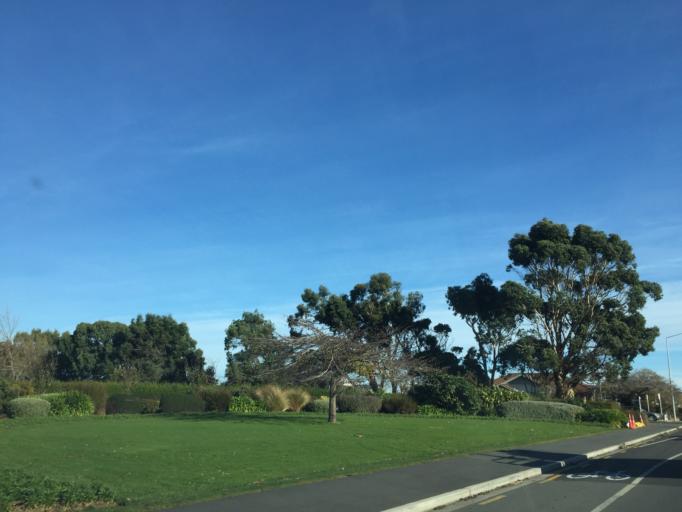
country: NZ
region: Southland
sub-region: Invercargill City
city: Invercargill
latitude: -46.4086
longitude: 168.3611
